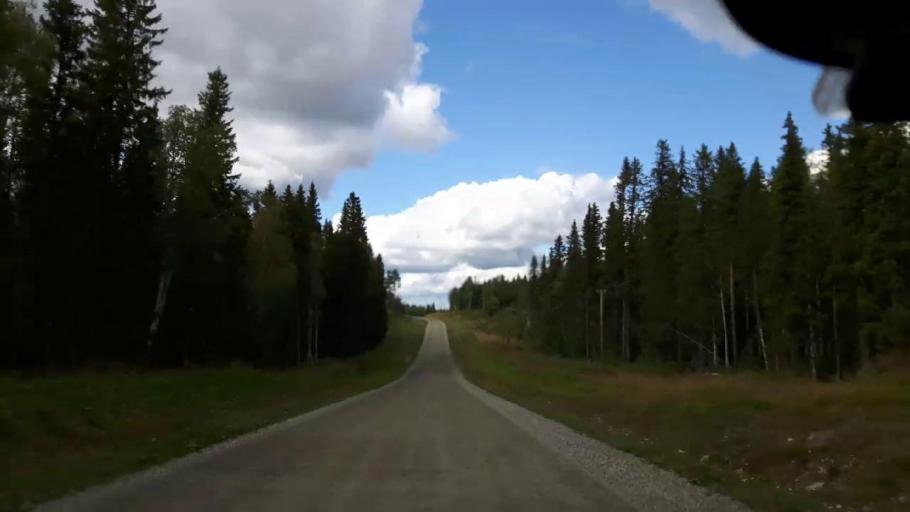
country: SE
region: Jaemtland
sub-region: Stroemsunds Kommun
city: Stroemsund
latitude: 63.3708
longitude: 15.5651
